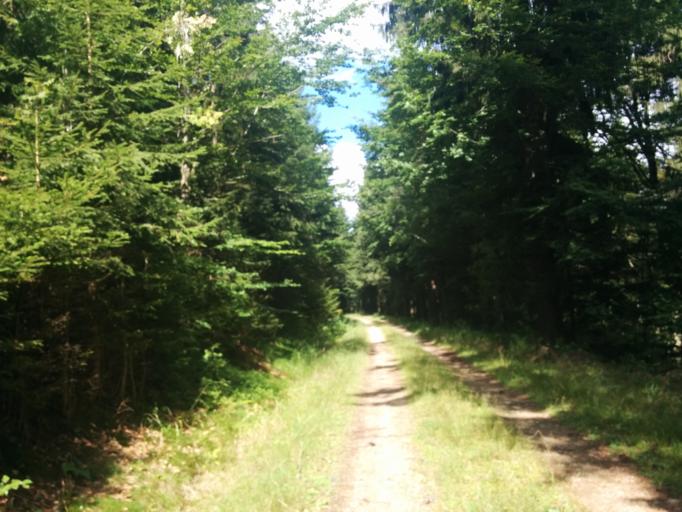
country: AT
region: Upper Austria
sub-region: Politischer Bezirk Rohrbach
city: Ulrichsberg
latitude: 48.7074
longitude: 13.9630
